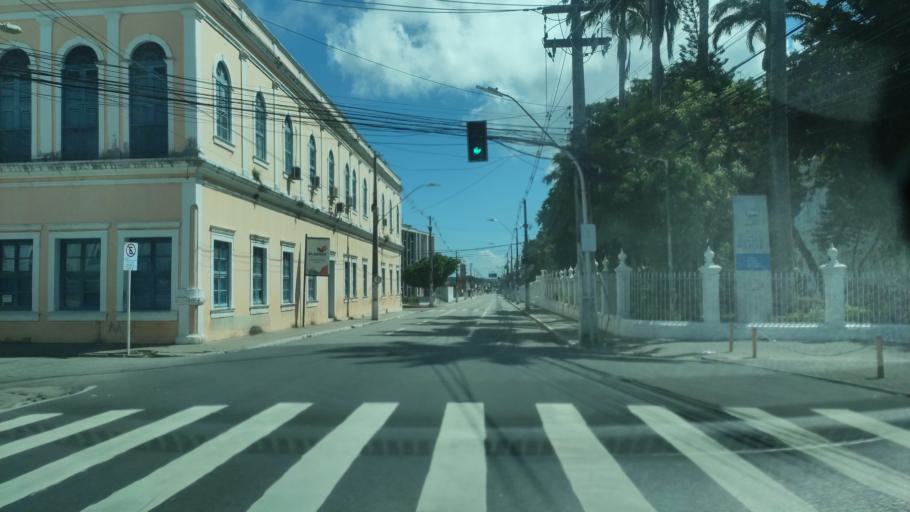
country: BR
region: Alagoas
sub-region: Maceio
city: Maceio
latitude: -9.6605
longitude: -35.7391
